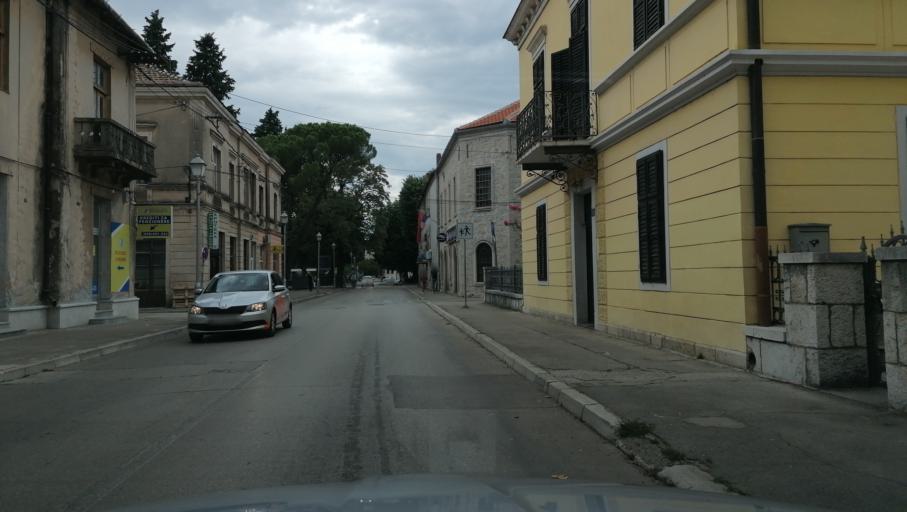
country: BA
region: Republika Srpska
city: Trebinje
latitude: 42.7108
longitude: 18.3449
